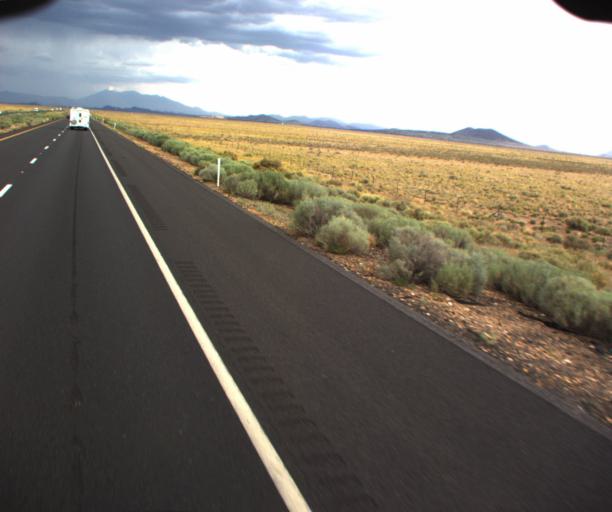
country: US
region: Arizona
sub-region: Coconino County
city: Flagstaff
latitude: 35.1389
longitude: -111.2100
